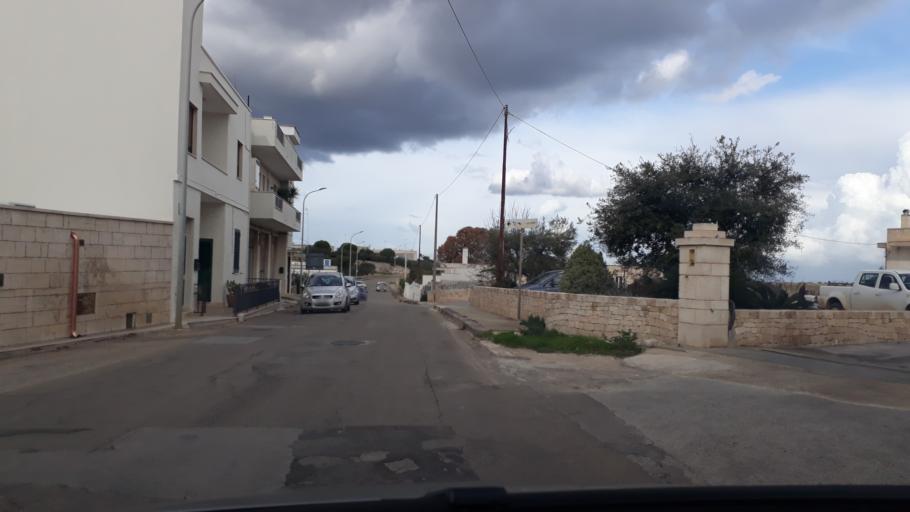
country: IT
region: Apulia
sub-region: Provincia di Brindisi
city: Cisternino
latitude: 40.7418
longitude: 17.4319
